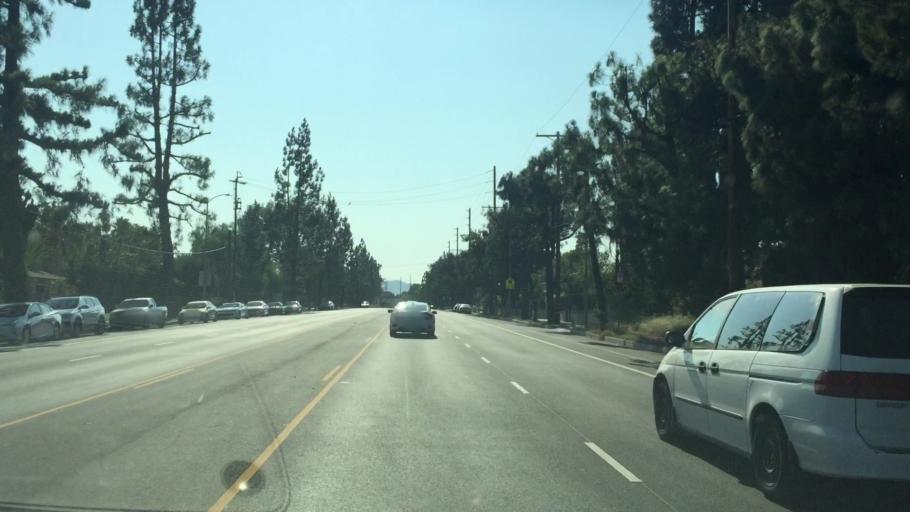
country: US
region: California
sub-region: Los Angeles County
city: Northridge
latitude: 34.2576
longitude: -118.5172
